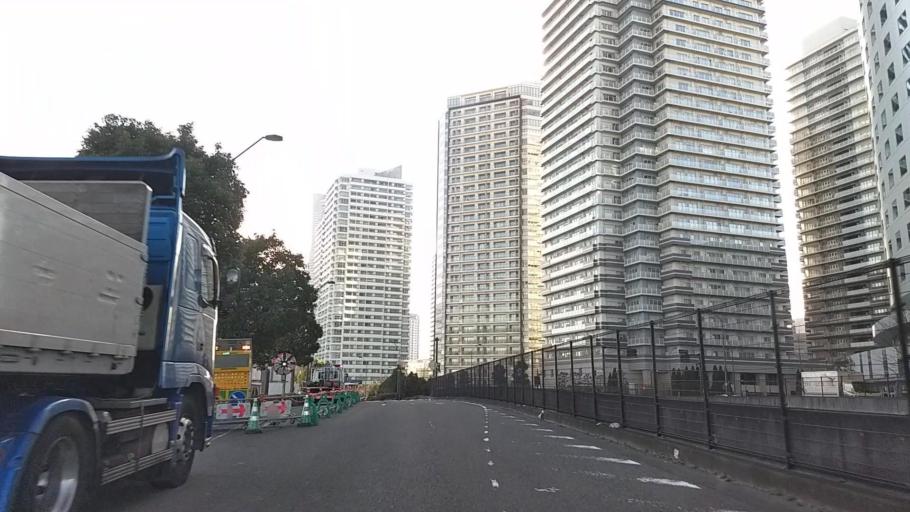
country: JP
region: Kanagawa
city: Yokohama
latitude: 35.4636
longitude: 139.6335
